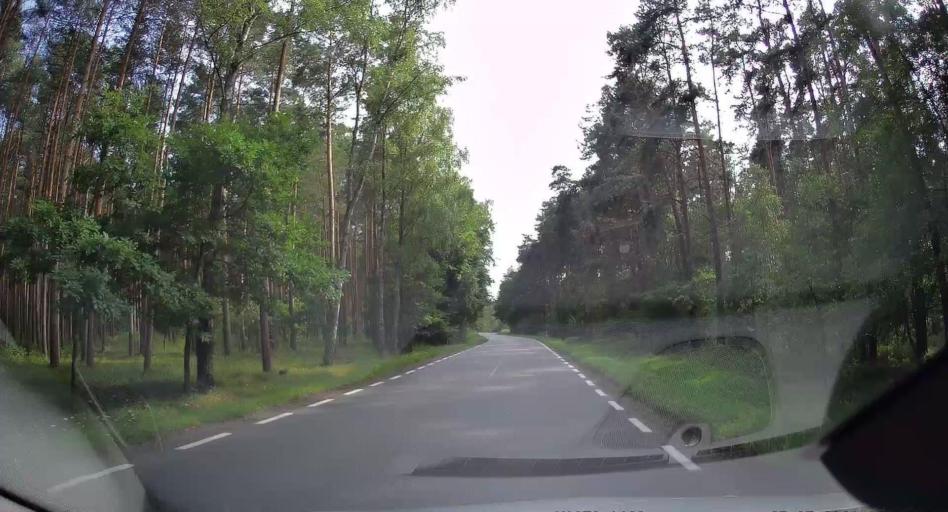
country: PL
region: Lodz Voivodeship
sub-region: Powiat tomaszowski
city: Inowlodz
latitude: 51.5416
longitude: 20.2350
